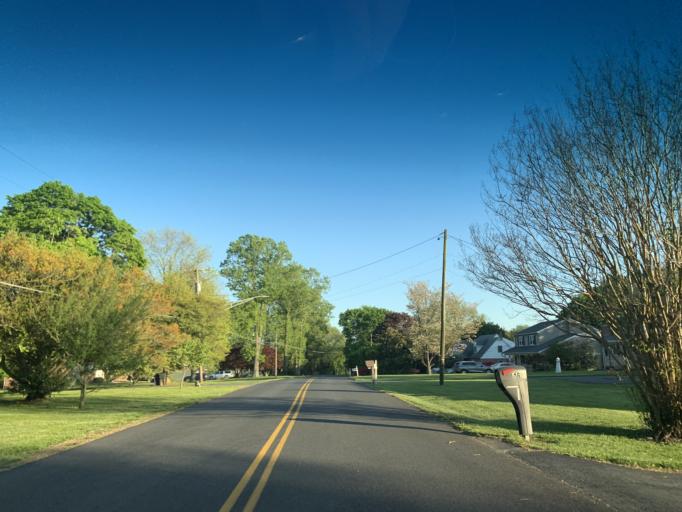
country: US
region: Maryland
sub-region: Harford County
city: Aberdeen
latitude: 39.5385
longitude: -76.1782
